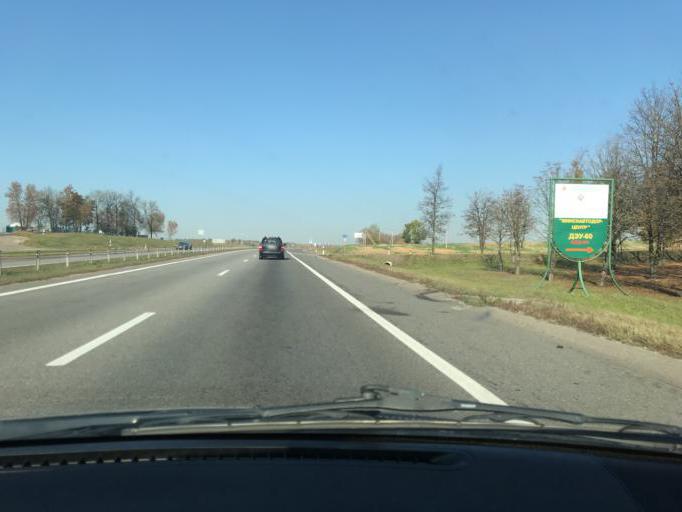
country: BY
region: Minsk
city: Samakhvalavichy
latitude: 53.7481
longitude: 27.5143
